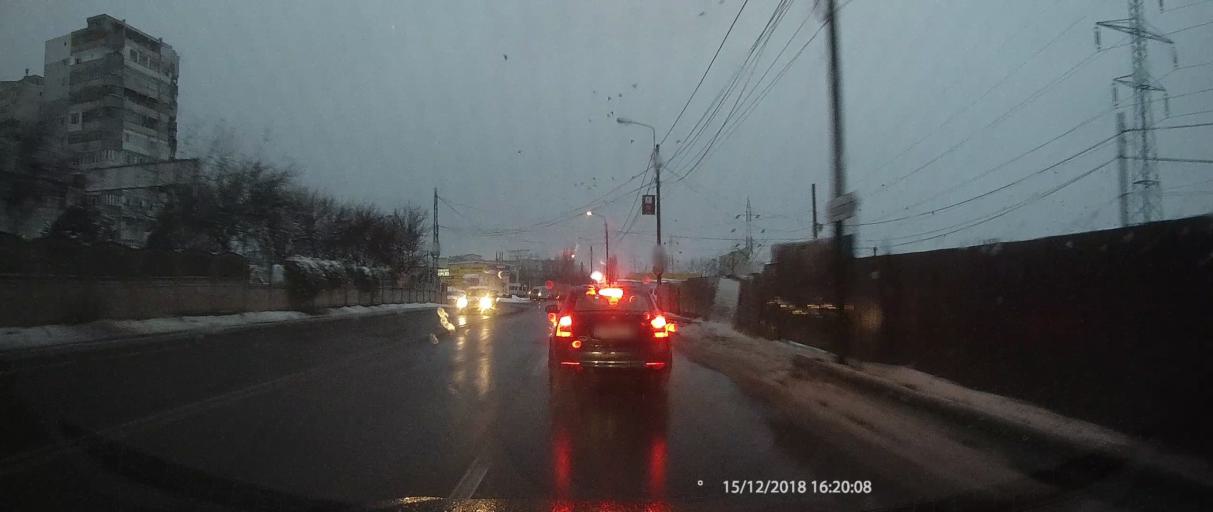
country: RO
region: Galati
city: Galati
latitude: 45.4148
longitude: 28.0049
